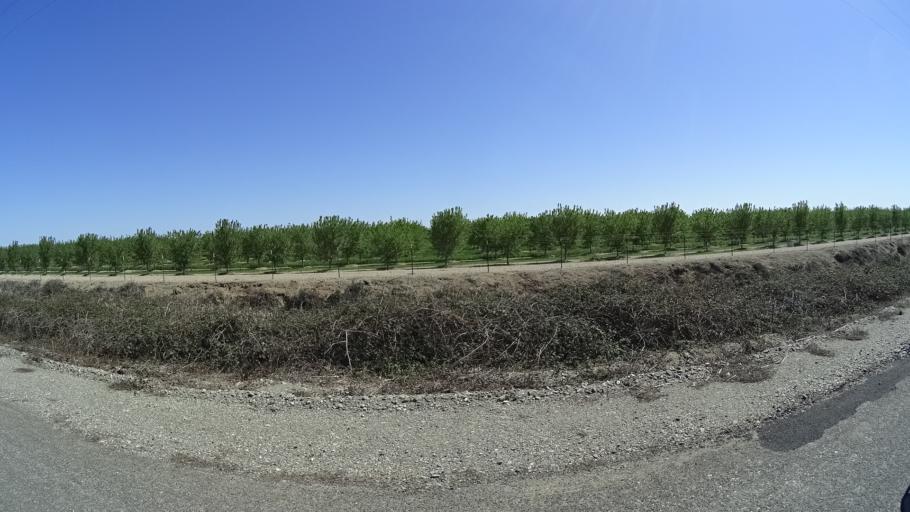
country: US
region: California
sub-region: Glenn County
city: Orland
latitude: 39.6722
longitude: -122.2343
